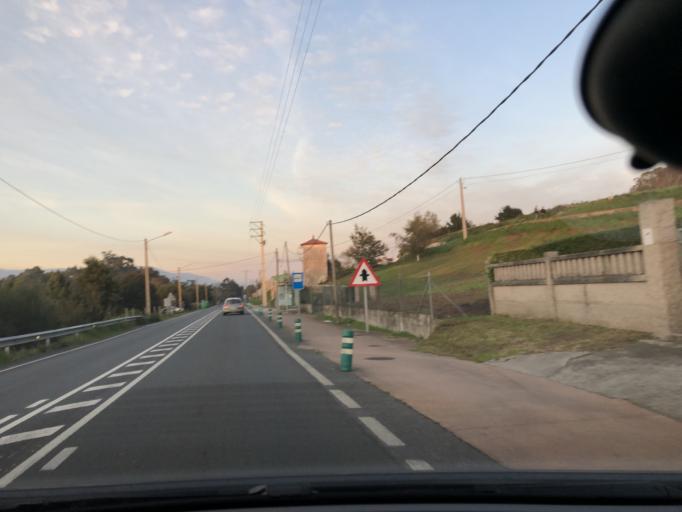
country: ES
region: Galicia
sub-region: Provincia de Pontevedra
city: Marin
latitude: 42.3798
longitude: -8.7243
